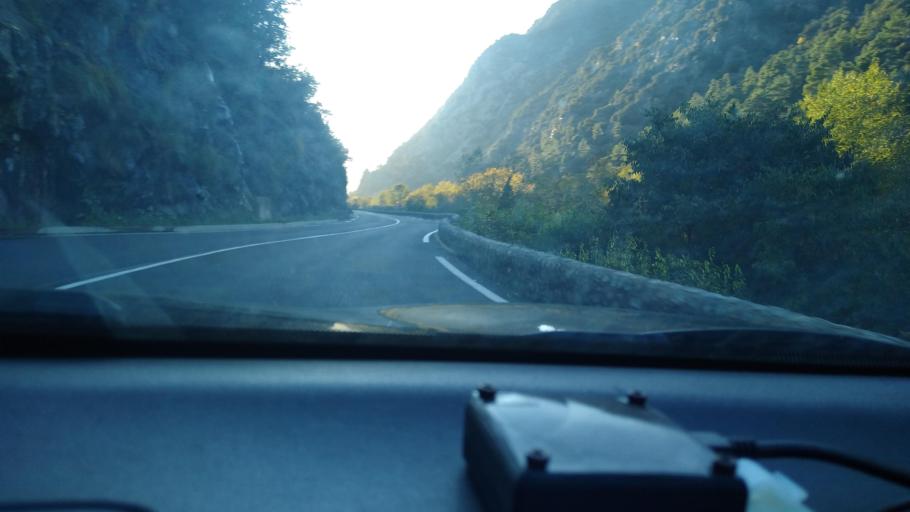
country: FR
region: Languedoc-Roussillon
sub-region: Departement des Pyrenees-Orientales
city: Vernet-les-Bains
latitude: 42.5284
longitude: 2.2458
